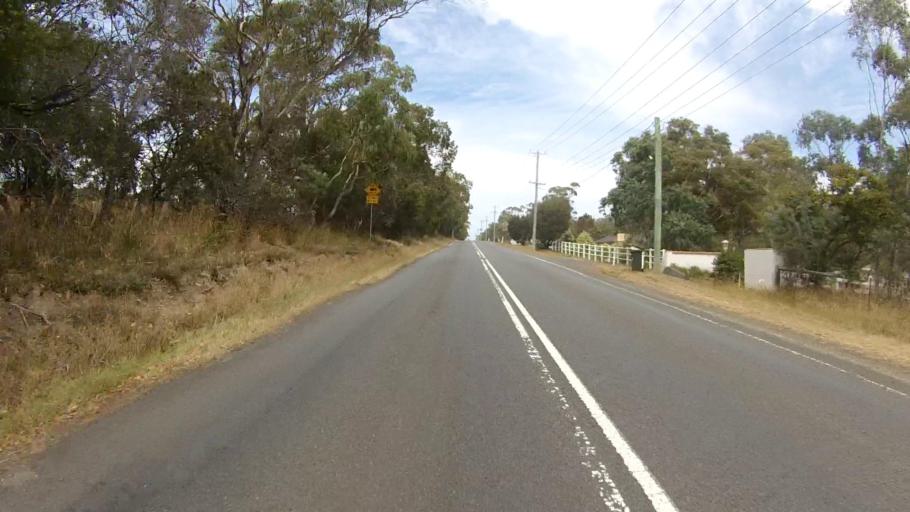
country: AU
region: Tasmania
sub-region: Clarence
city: Acton Park
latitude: -42.8688
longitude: 147.4840
